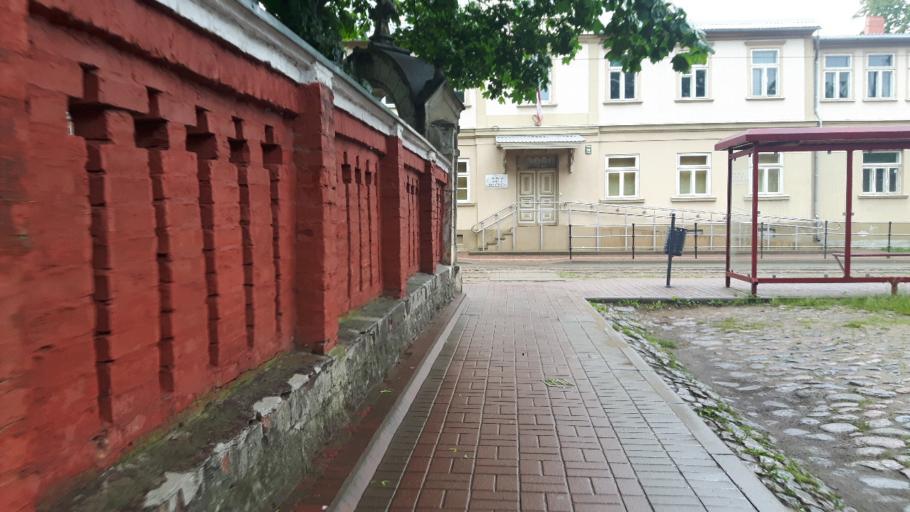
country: LV
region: Liepaja
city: Liepaja
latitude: 56.5053
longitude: 21.0071
